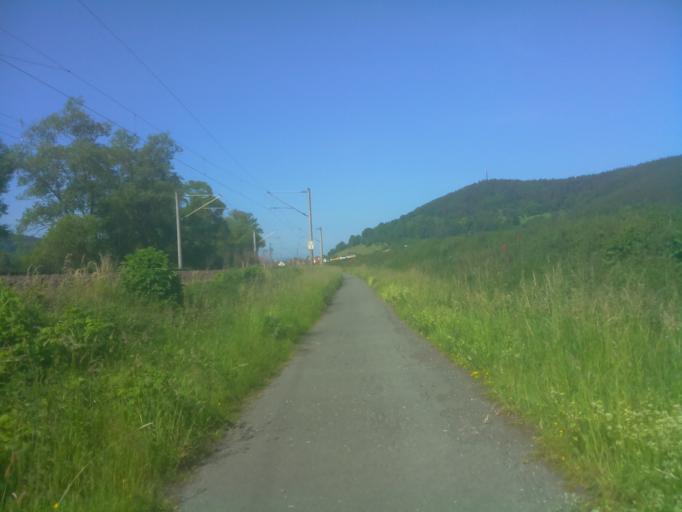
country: DE
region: Thuringia
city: Orlamunde
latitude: 50.7476
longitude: 11.4871
